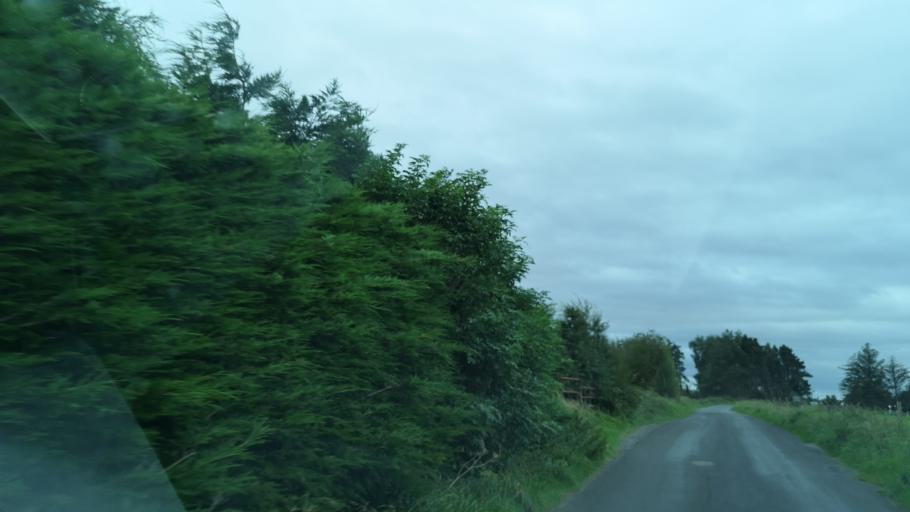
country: IE
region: Leinster
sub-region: Uibh Fhaili
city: Ferbane
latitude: 53.2098
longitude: -7.7237
